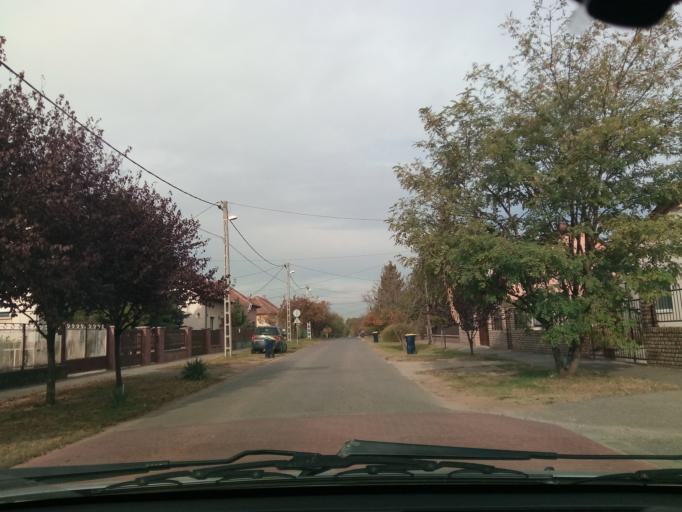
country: HU
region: Budapest
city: Budapest XVIII. keruelet
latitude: 47.4360
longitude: 19.2153
